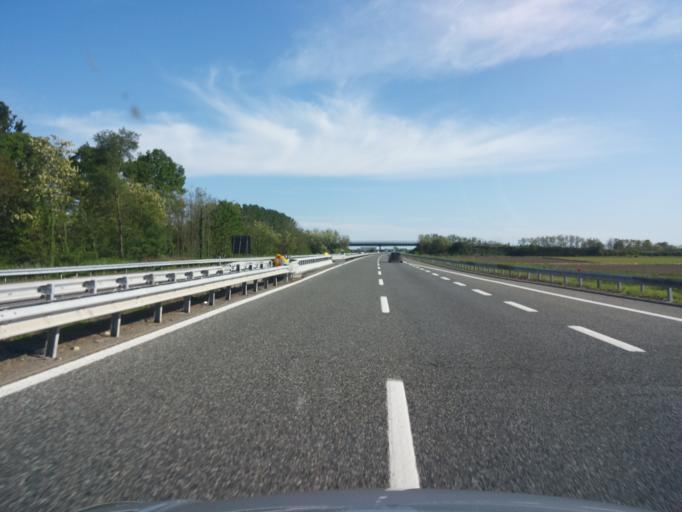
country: IT
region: Piedmont
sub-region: Provincia di Novara
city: Landiona
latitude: 45.5001
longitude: 8.4377
